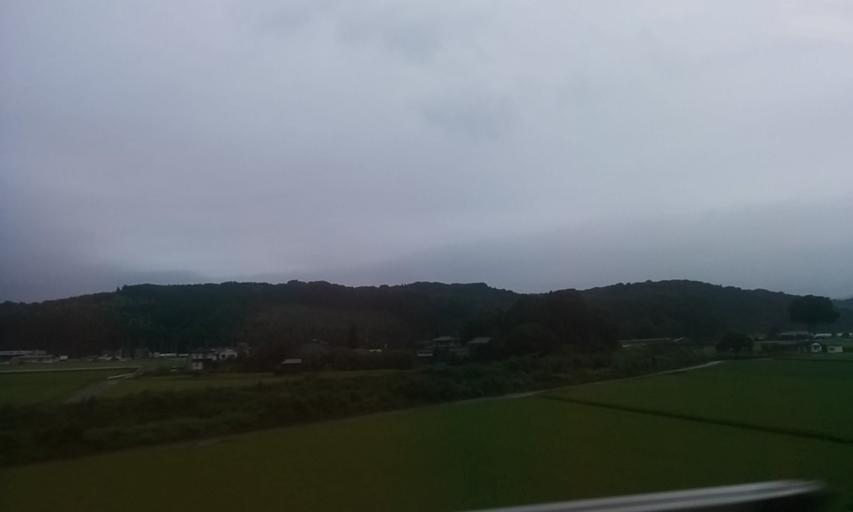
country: JP
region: Tochigi
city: Utsunomiya-shi
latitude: 36.6146
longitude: 139.9075
